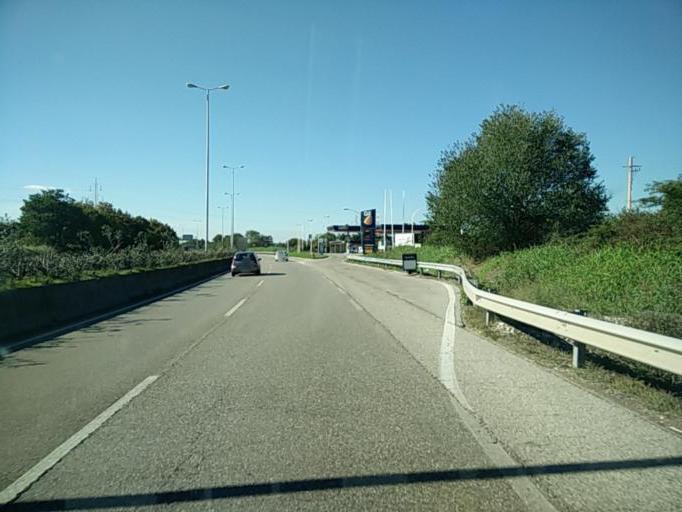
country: IT
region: Veneto
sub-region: Provincia di Verona
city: Caselle
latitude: 45.4317
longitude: 10.9242
